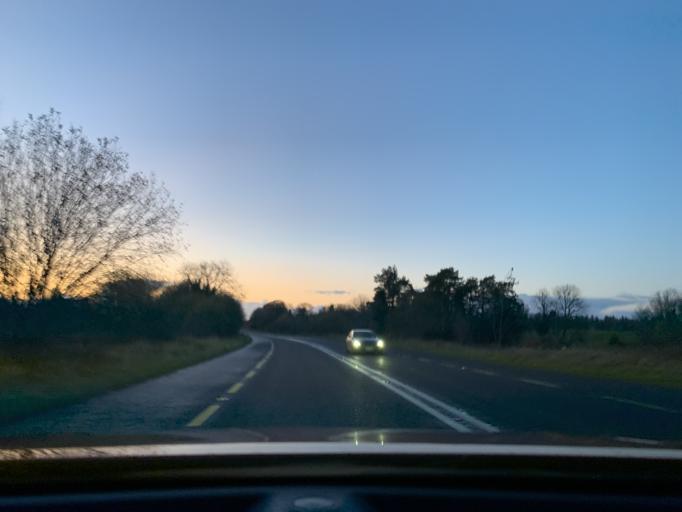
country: IE
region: Connaught
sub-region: County Leitrim
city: Carrick-on-Shannon
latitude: 53.9576
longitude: -8.1651
